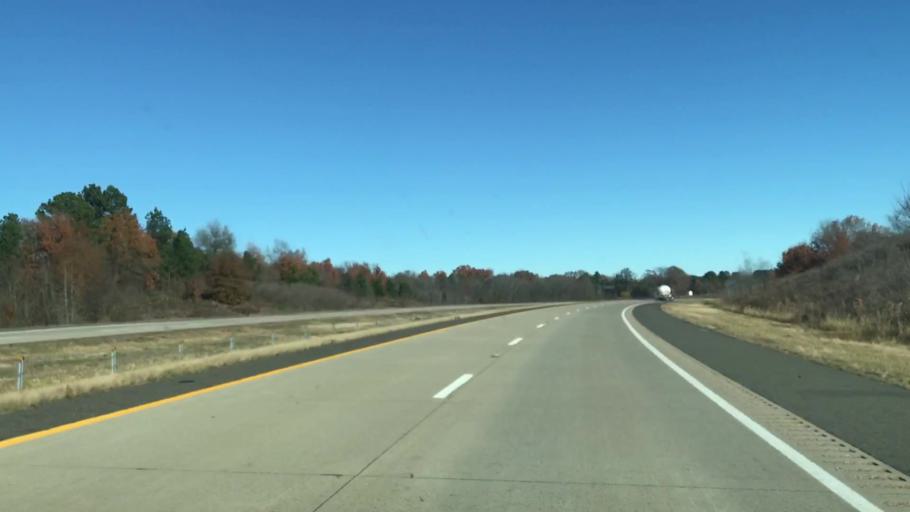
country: US
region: Texas
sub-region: Cass County
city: Queen City
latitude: 33.1547
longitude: -93.8897
